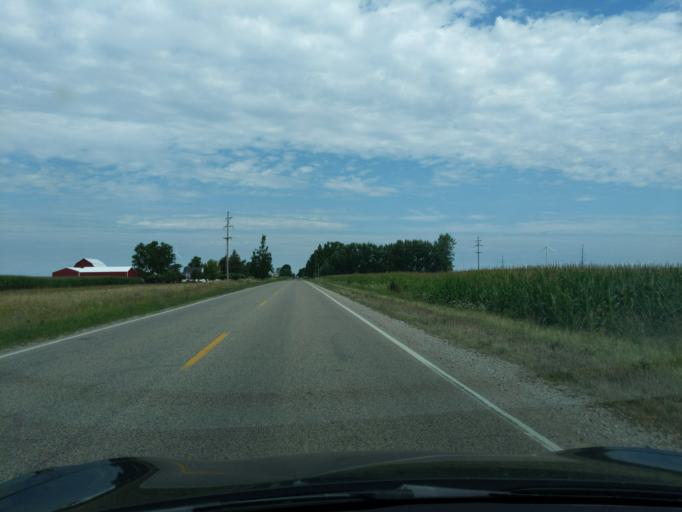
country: US
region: Michigan
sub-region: Gratiot County
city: Breckenridge
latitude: 43.3793
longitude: -84.4294
